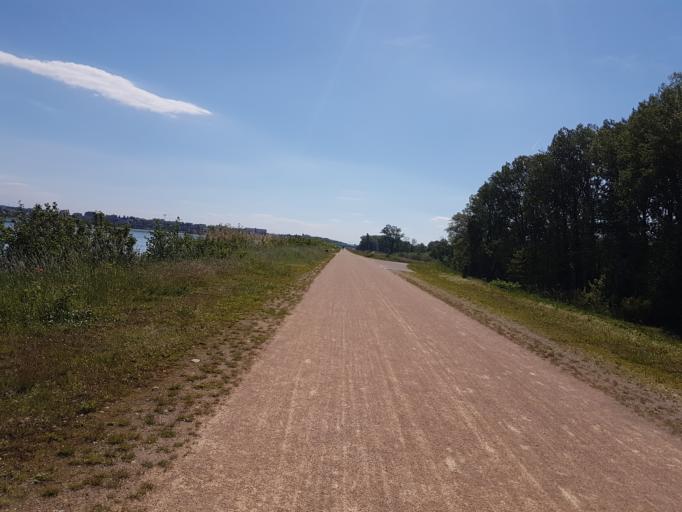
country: FR
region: Rhone-Alpes
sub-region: Departement du Rhone
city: Decines-Charpieu
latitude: 45.7910
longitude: 4.9815
